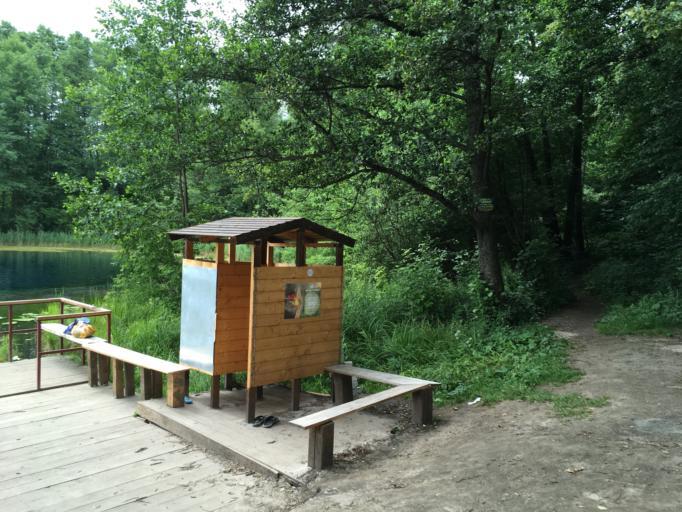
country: RU
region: Tatarstan
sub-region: Gorod Kazan'
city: Kazan
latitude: 55.9069
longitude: 49.1548
